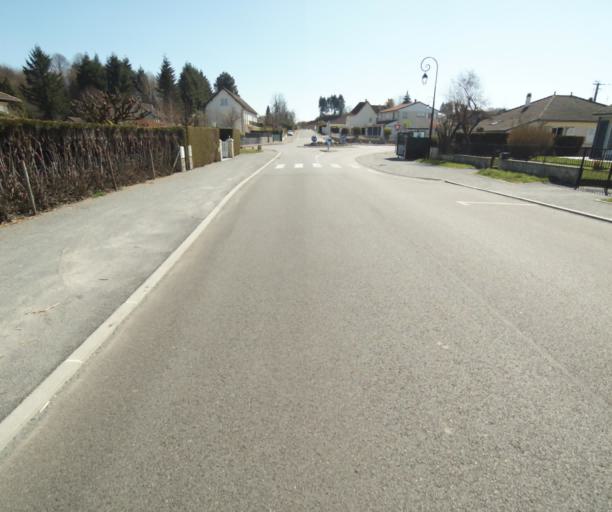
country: FR
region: Limousin
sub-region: Departement de la Correze
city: Saint-Mexant
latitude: 45.2815
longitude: 1.6596
